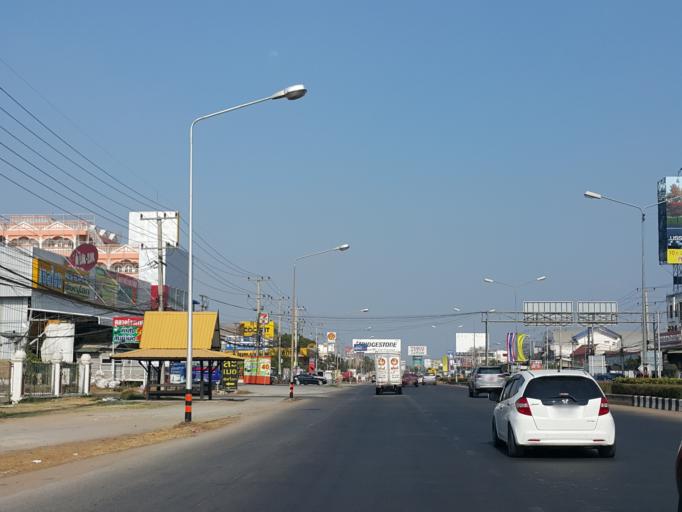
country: TH
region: Phitsanulok
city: Phitsanulok
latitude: 16.8183
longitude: 100.2899
